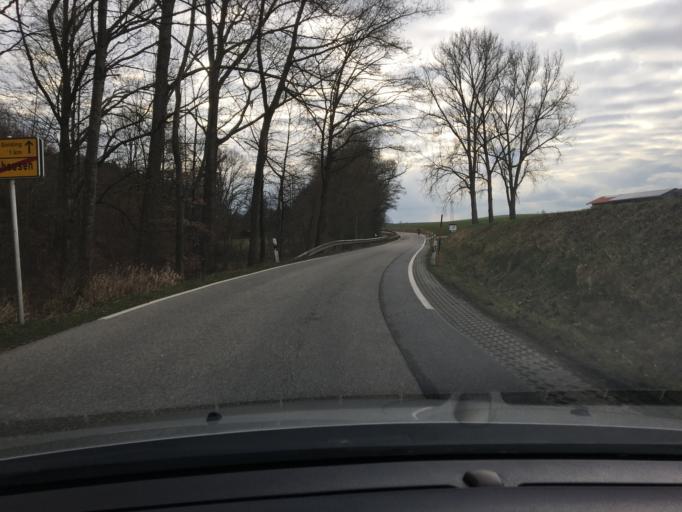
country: DE
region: Bavaria
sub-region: Lower Bavaria
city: Kumhausen
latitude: 48.5085
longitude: 12.1551
